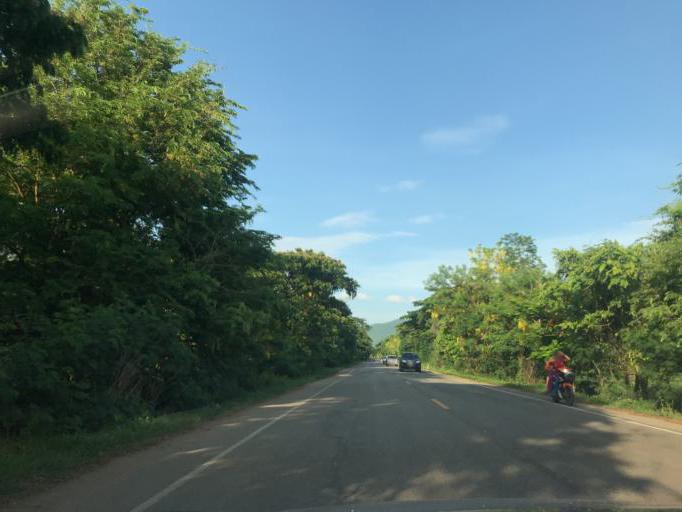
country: TH
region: Phayao
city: Phu Kam Yao
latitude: 19.3128
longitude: 100.0081
